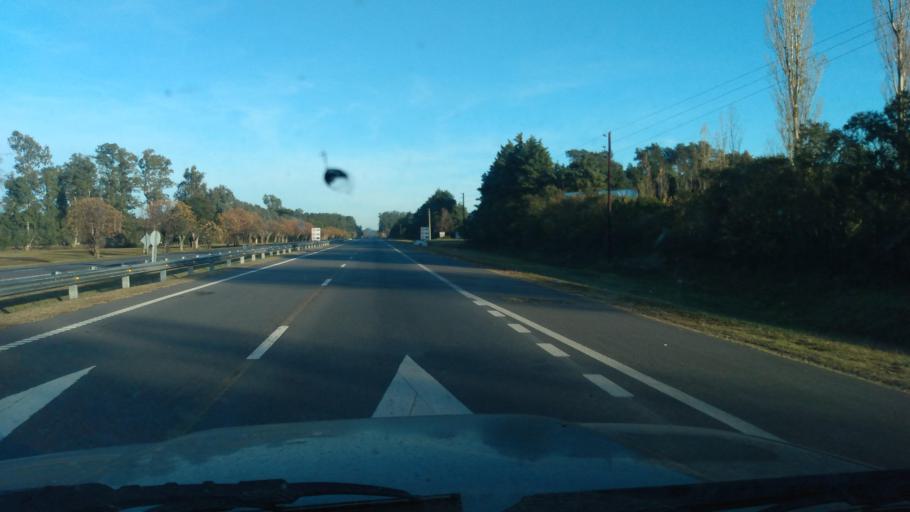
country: AR
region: Buenos Aires
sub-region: Partido de Lujan
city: Lujan
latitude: -34.5455
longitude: -59.2156
